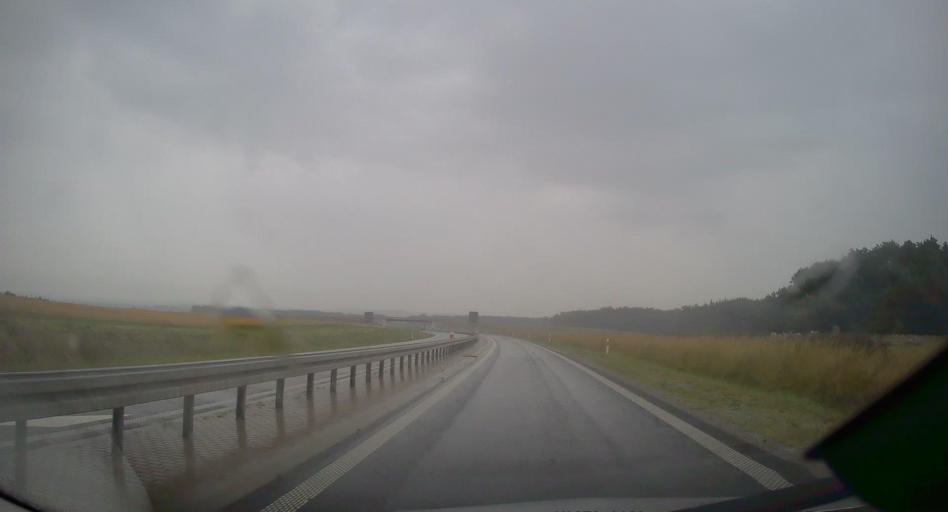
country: PL
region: Opole Voivodeship
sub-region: Powiat nyski
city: Nysa
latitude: 50.4454
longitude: 17.4067
